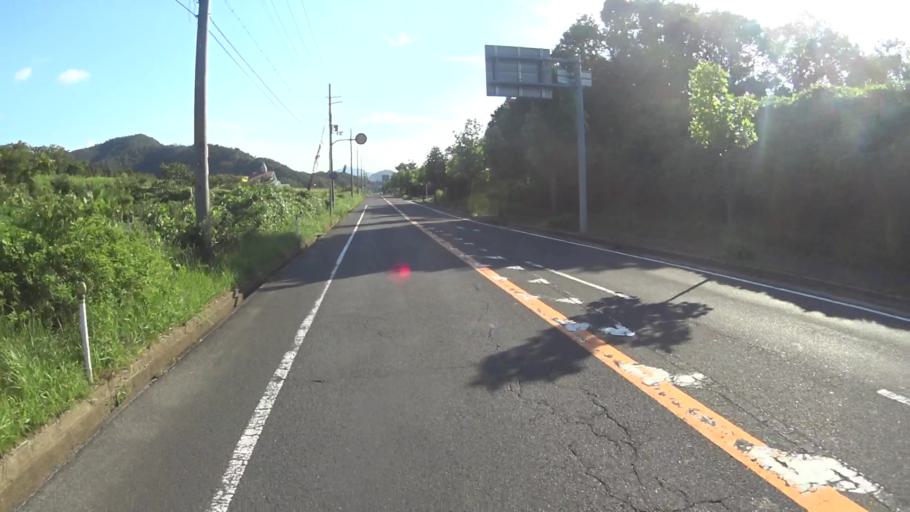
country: JP
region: Hyogo
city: Toyooka
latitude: 35.6336
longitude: 134.9328
